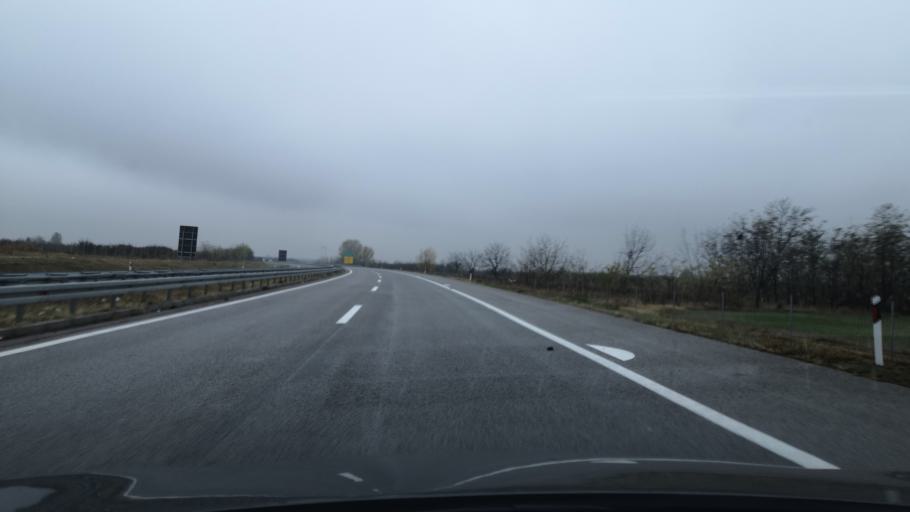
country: HU
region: Csongrad
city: Morahalom
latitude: 46.1617
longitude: 19.9455
